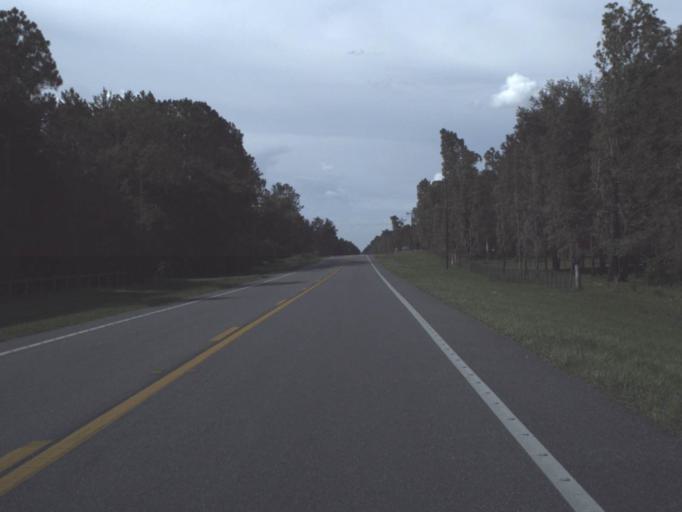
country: US
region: Florida
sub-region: Alachua County
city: High Springs
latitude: 29.8782
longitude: -82.8597
